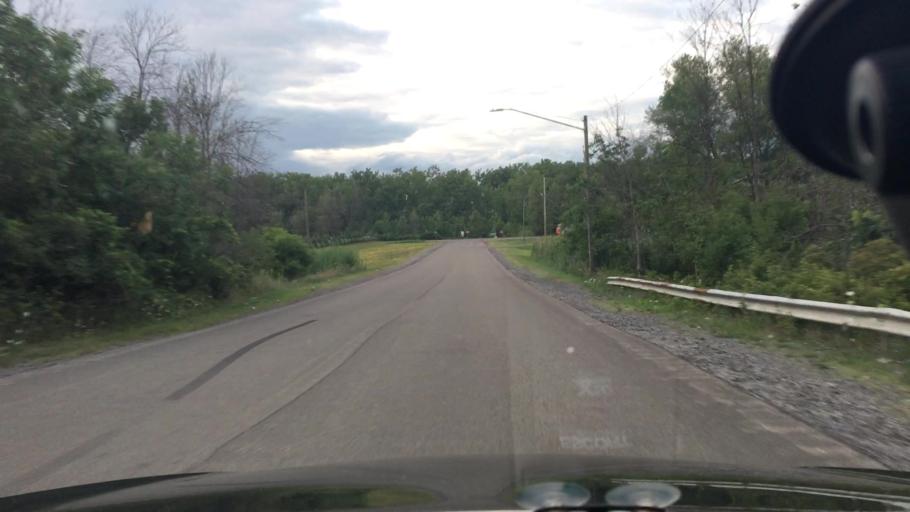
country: US
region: New York
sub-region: Erie County
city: West Seneca
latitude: 42.8445
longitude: -78.7648
